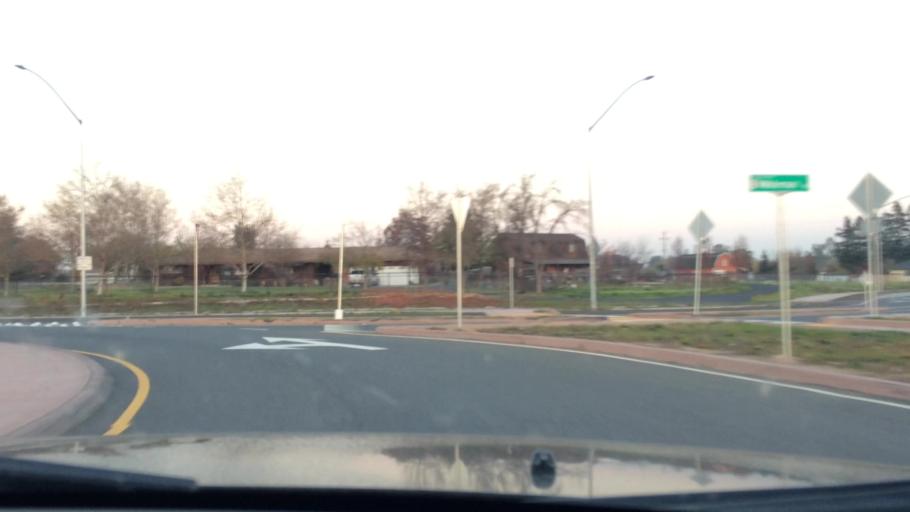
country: US
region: California
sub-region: Sacramento County
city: Vineyard
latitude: 38.4383
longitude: -121.3527
